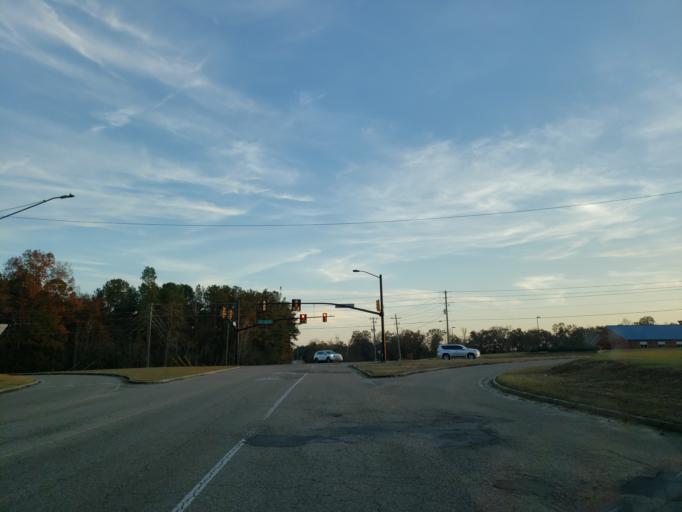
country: US
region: Mississippi
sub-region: Forrest County
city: Hattiesburg
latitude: 31.2910
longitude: -89.3135
